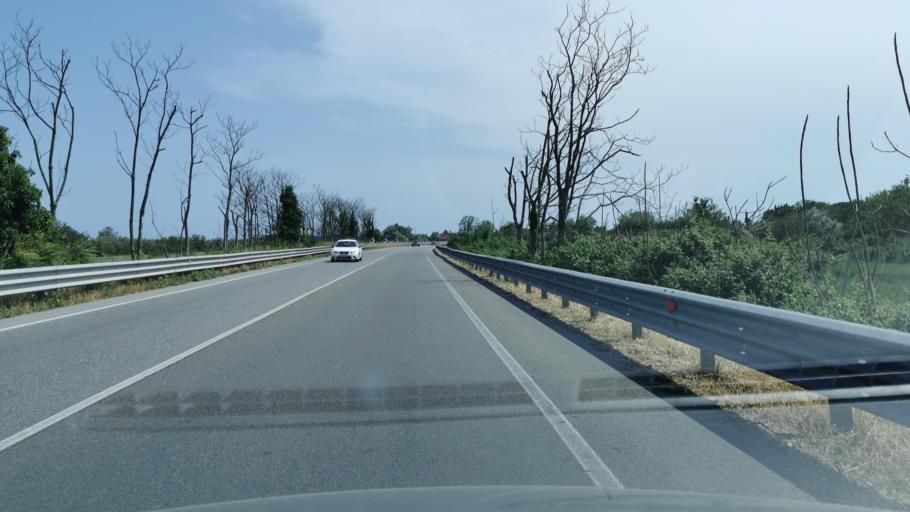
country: IT
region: Emilia-Romagna
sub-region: Provincia di Ravenna
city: Marina Romea
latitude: 44.5859
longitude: 12.2530
